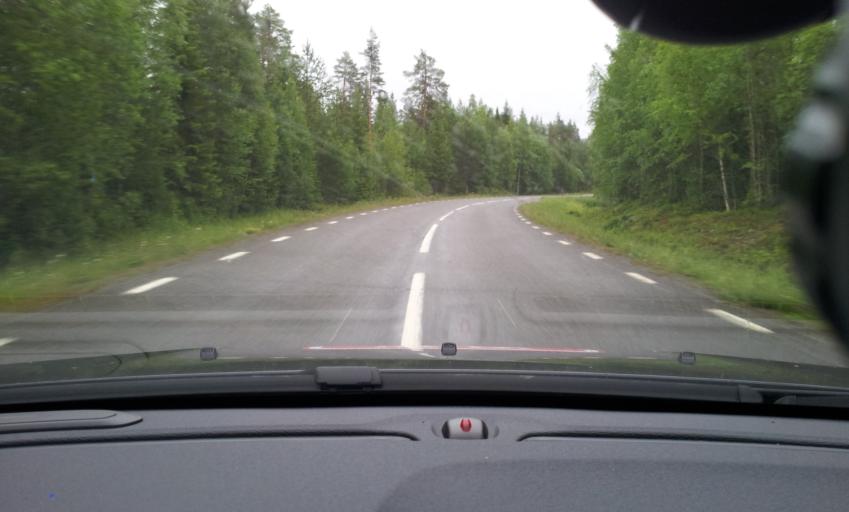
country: SE
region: Jaemtland
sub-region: Stroemsunds Kommun
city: Stroemsund
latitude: 63.3940
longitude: 15.6616
